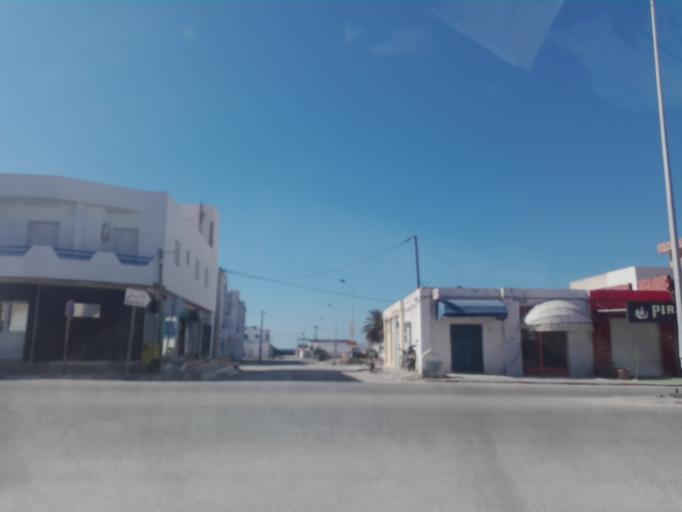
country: TN
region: Safaqis
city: Al Qarmadah
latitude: 34.7051
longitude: 11.2017
